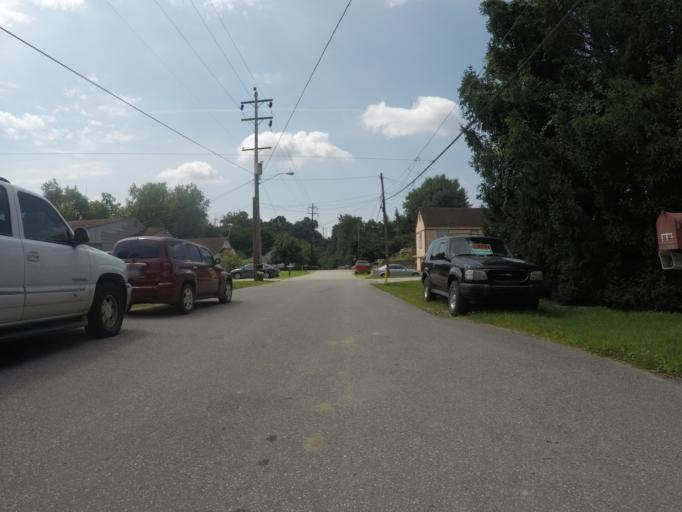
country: US
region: West Virginia
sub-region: Cabell County
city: Pea Ridge
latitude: 38.4160
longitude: -82.3567
